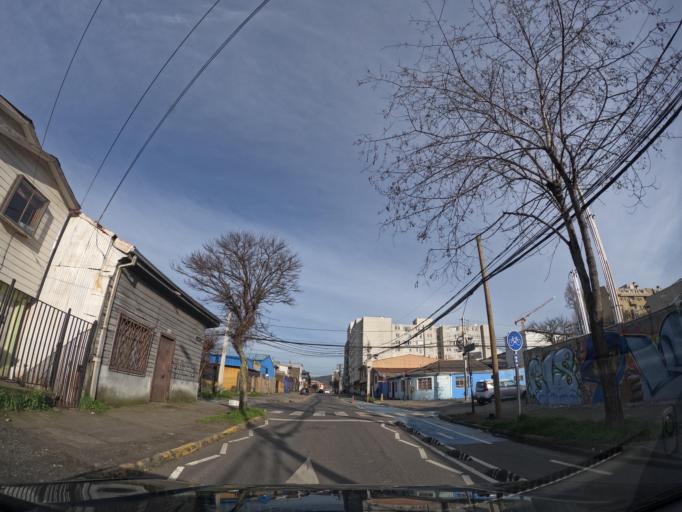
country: CL
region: Biobio
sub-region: Provincia de Concepcion
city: Concepcion
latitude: -36.8164
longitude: -73.0481
